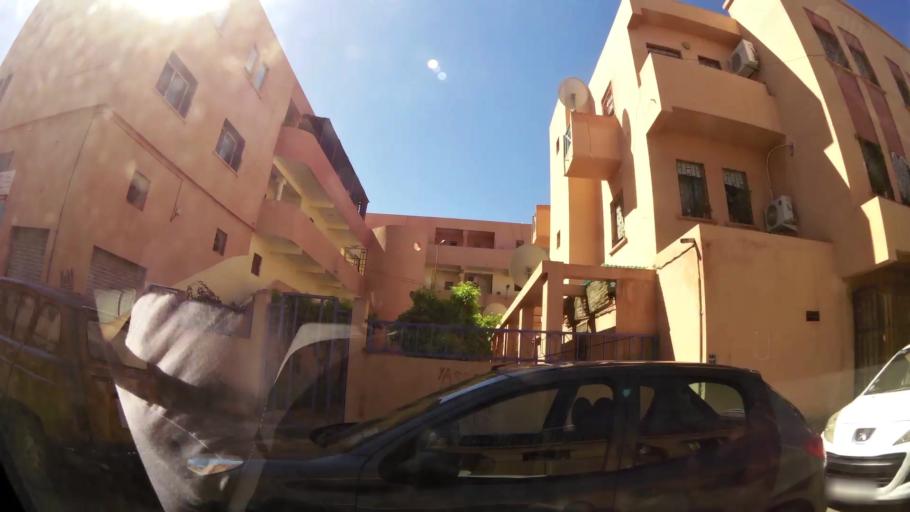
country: MA
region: Marrakech-Tensift-Al Haouz
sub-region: Marrakech
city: Marrakesh
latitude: 31.6456
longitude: -7.9846
